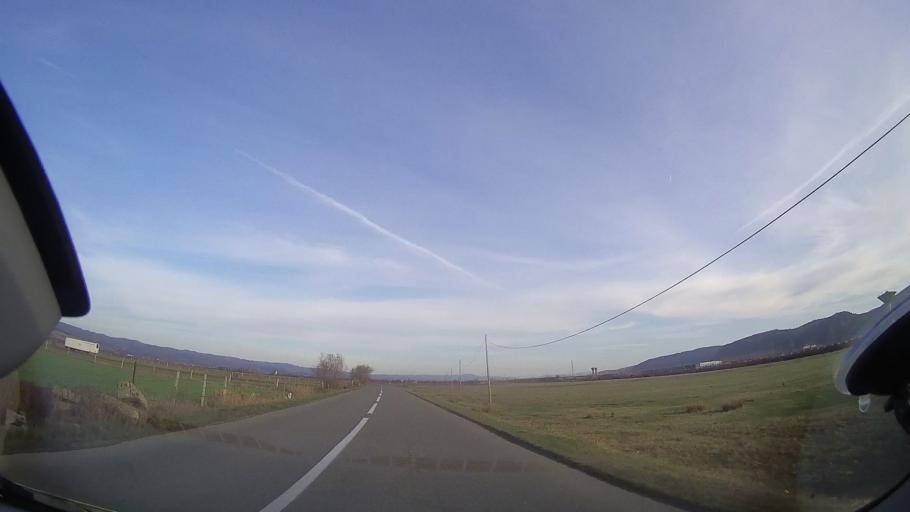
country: RO
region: Bihor
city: Lugasu de Jos
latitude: 47.0439
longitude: 22.3357
